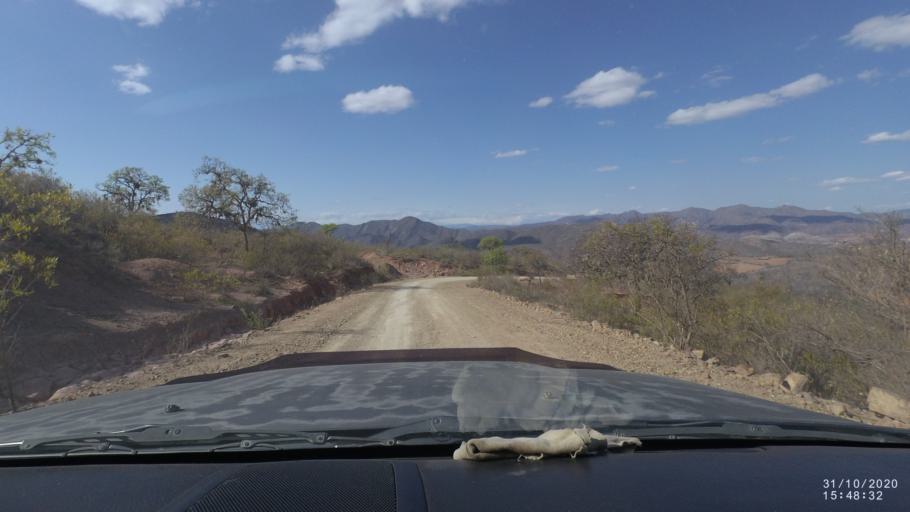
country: BO
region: Chuquisaca
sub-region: Provincia Zudanez
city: Mojocoya
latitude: -18.3114
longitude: -64.7104
